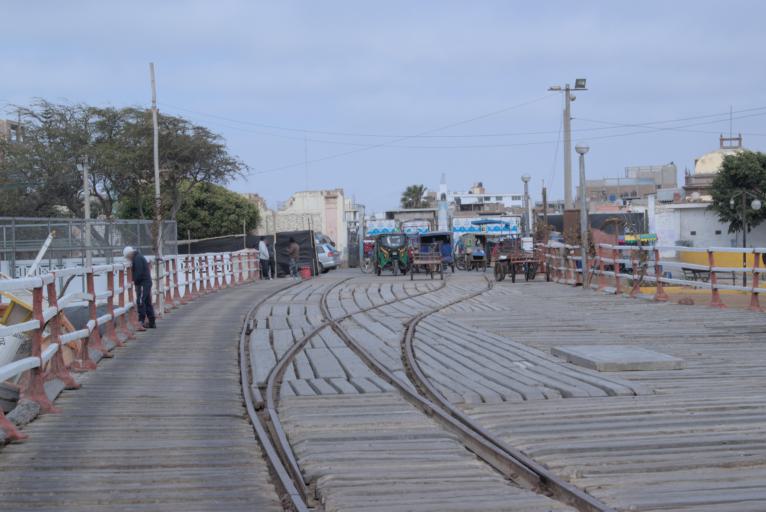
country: PE
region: La Libertad
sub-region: Provincia de Pacasmayo
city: Pacasmayo
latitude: -7.3988
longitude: -79.5717
